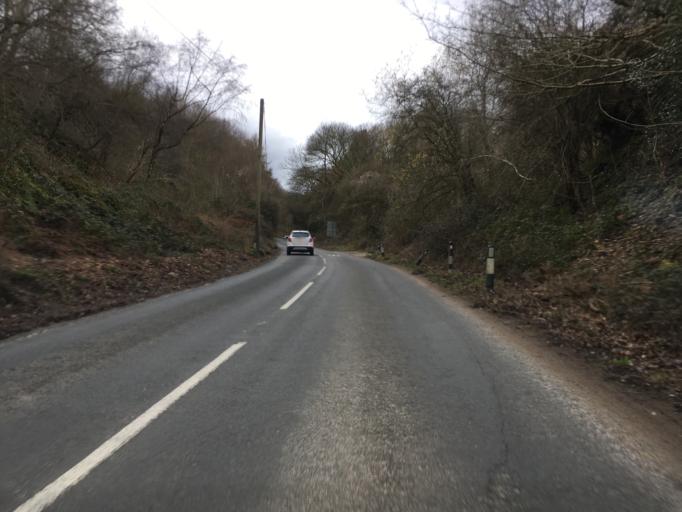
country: GB
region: England
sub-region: Gloucestershire
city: Coleford
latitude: 51.7998
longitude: -2.5862
